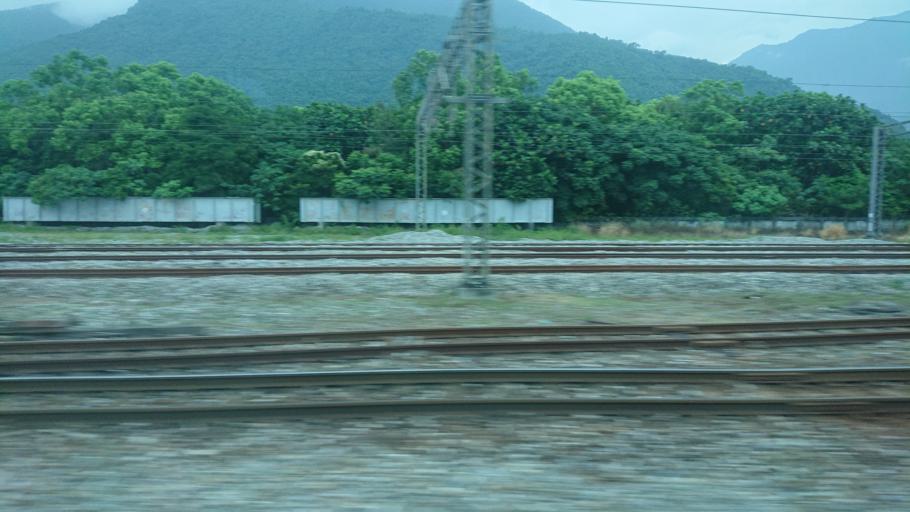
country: TW
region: Taiwan
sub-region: Hualien
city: Hualian
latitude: 24.1264
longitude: 121.6396
